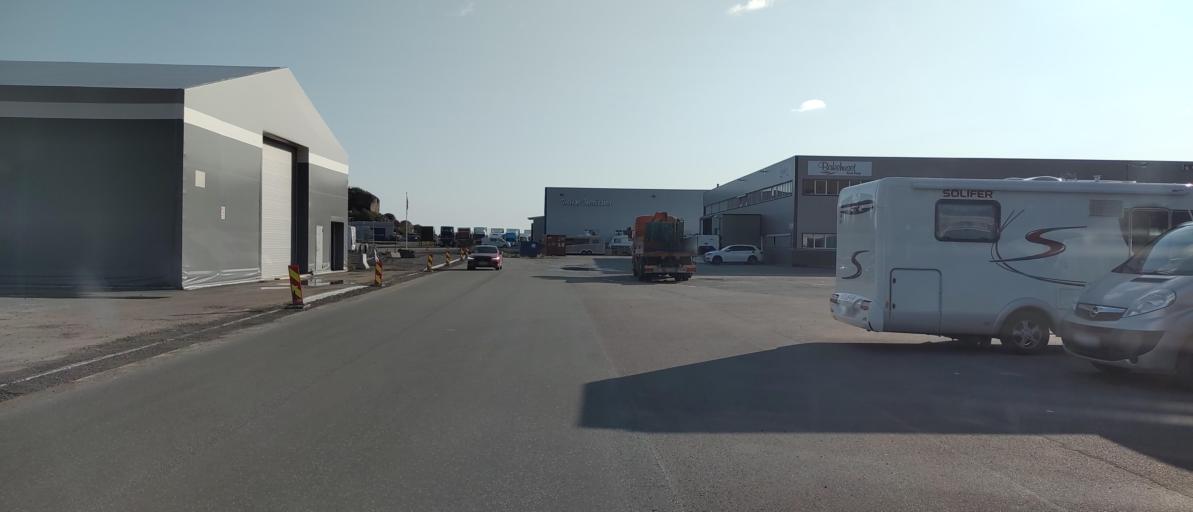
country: NO
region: Nordland
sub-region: Vagan
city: Svolvaer
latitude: 68.2283
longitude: 14.5566
